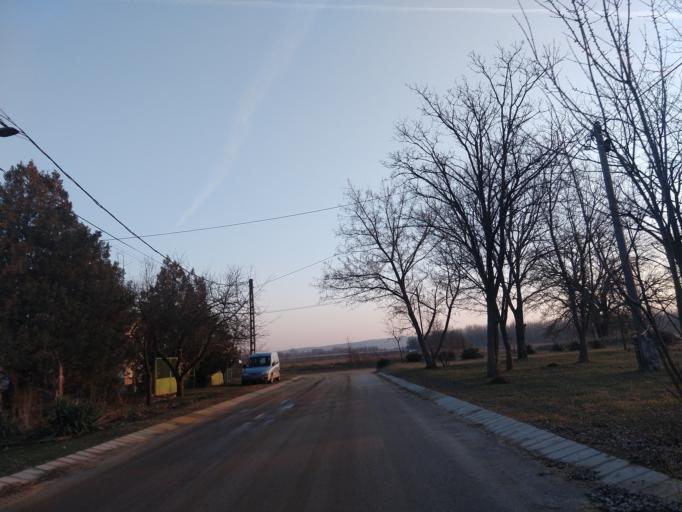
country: HU
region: Pest
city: Veresegyhaz
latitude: 47.6339
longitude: 19.2755
